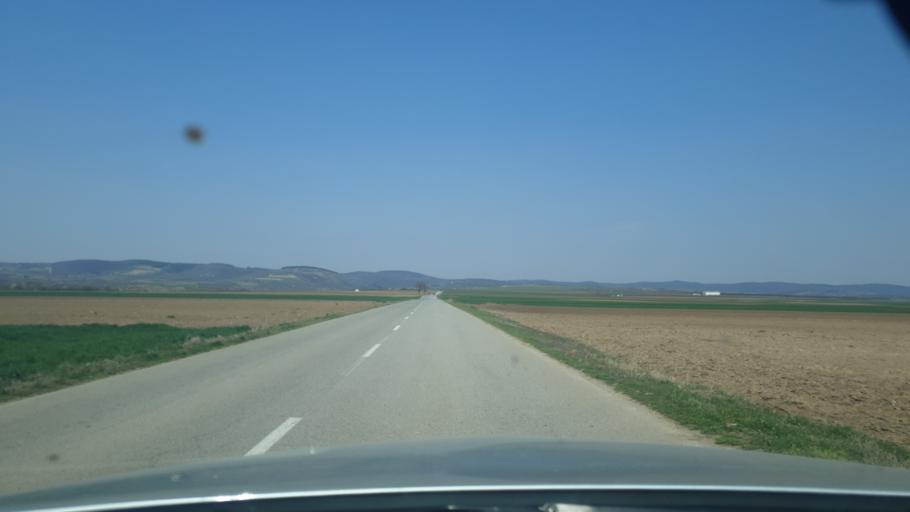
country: RS
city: Vrdnik
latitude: 45.0726
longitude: 19.7698
